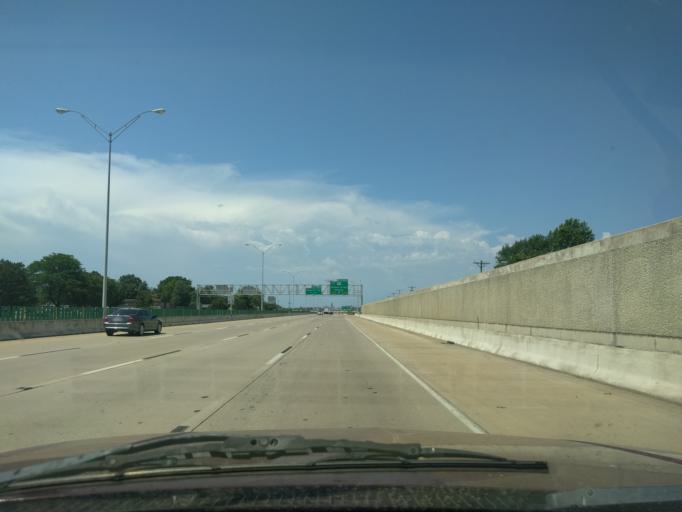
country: US
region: Oklahoma
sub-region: Tulsa County
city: Broken Arrow
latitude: 36.1439
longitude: -95.8540
